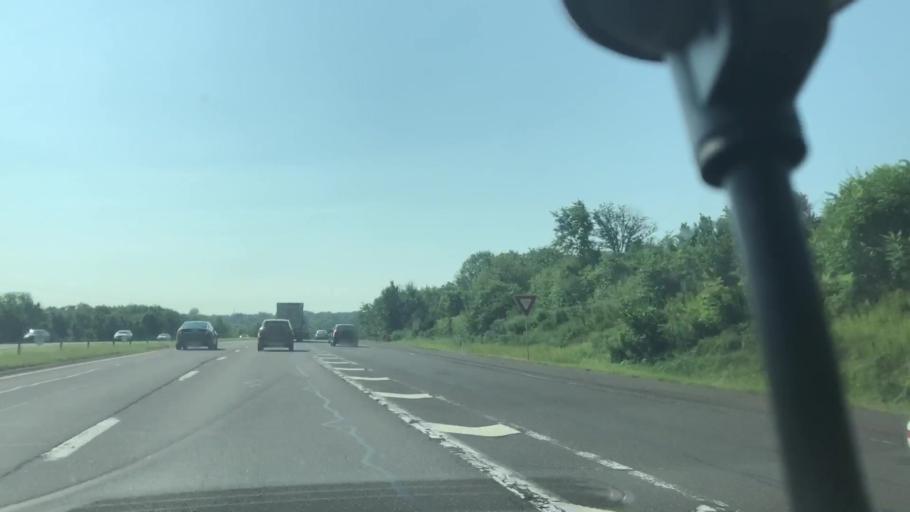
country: US
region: Pennsylvania
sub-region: Montgomery County
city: Royersford
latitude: 40.1931
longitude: -75.5225
